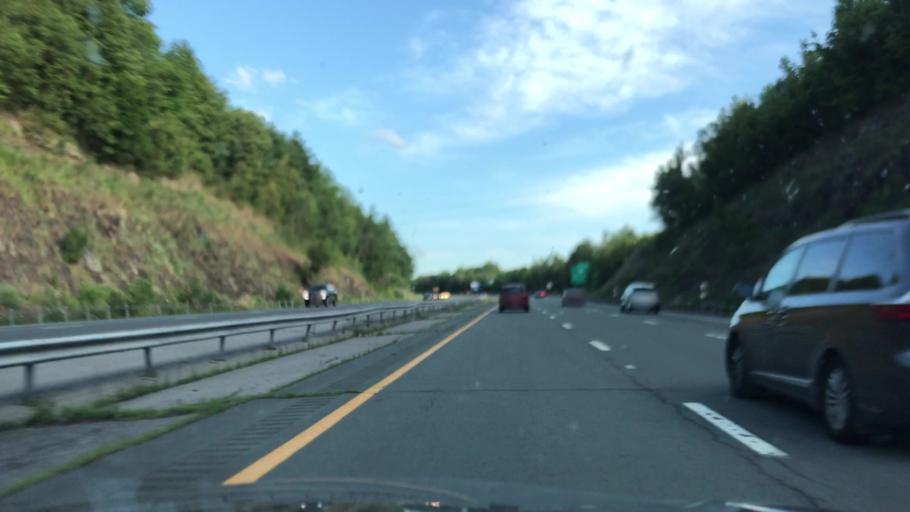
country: US
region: New York
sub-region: Sullivan County
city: Monticello
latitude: 41.6738
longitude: -74.7140
